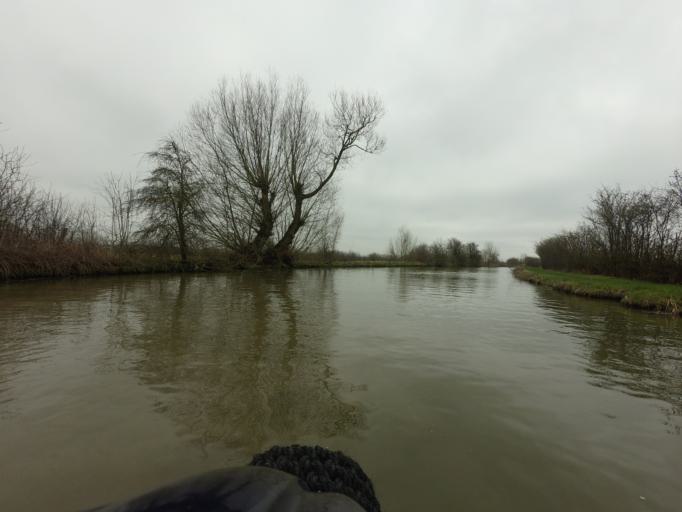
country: GB
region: England
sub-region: Central Bedfordshire
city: Leighton Buzzard
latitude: 51.8850
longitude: -0.6554
